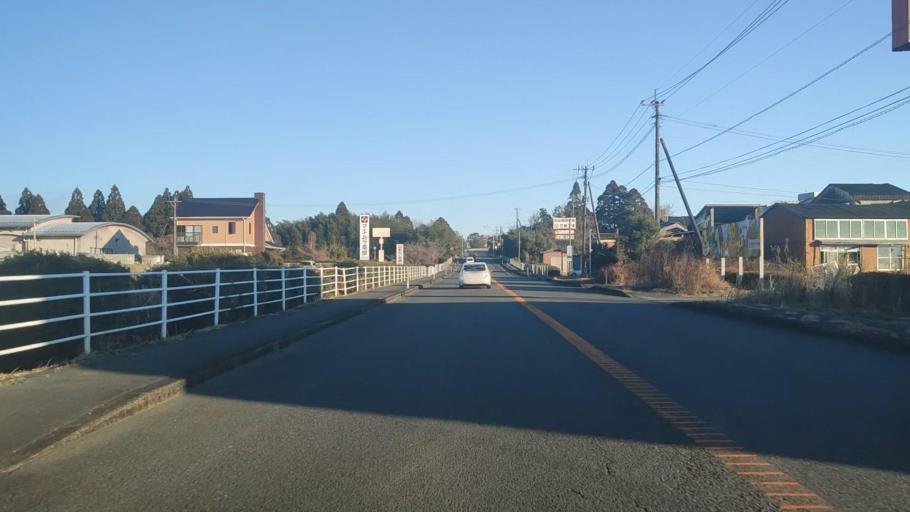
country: JP
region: Miyazaki
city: Takanabe
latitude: 32.1895
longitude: 131.5239
